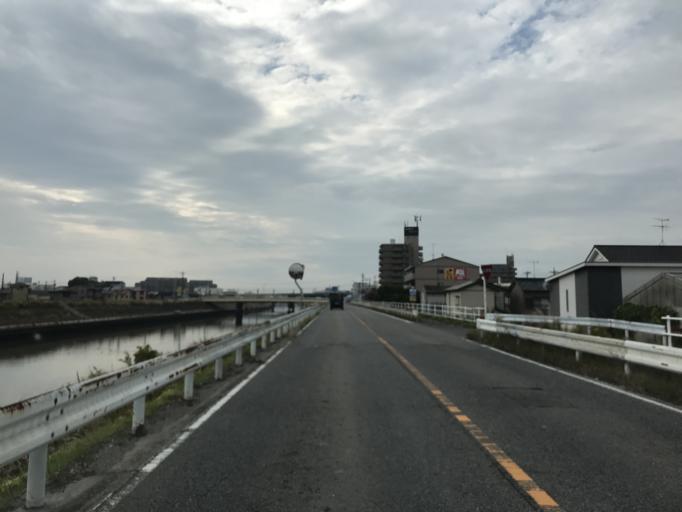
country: JP
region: Aichi
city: Nagoya-shi
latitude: 35.2080
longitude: 136.8597
